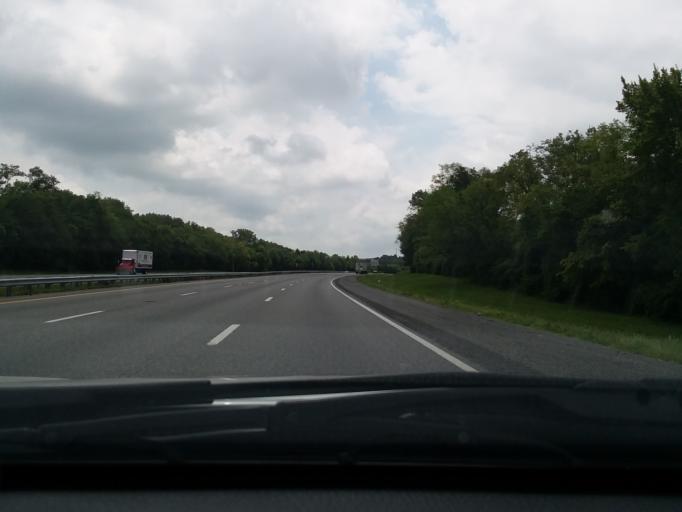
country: US
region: Tennessee
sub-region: Davidson County
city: Goodlettsville
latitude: 36.3177
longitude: -86.7022
